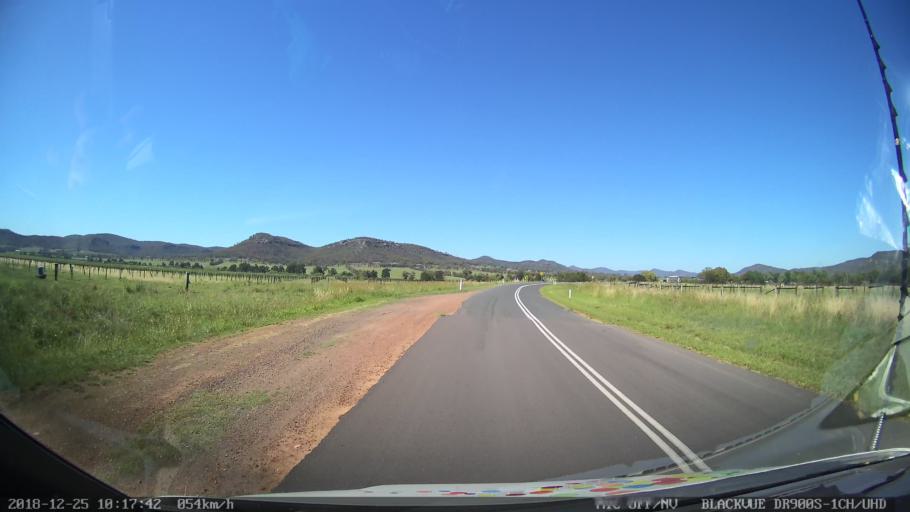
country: AU
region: New South Wales
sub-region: Muswellbrook
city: Denman
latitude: -32.3442
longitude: 150.5771
